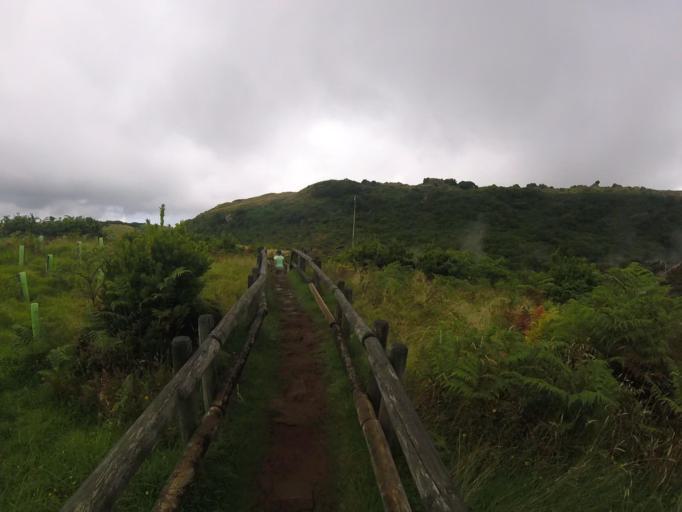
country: PT
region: Azores
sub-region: Praia da Vitoria
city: Biscoitos
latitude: 38.7295
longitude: -27.2326
